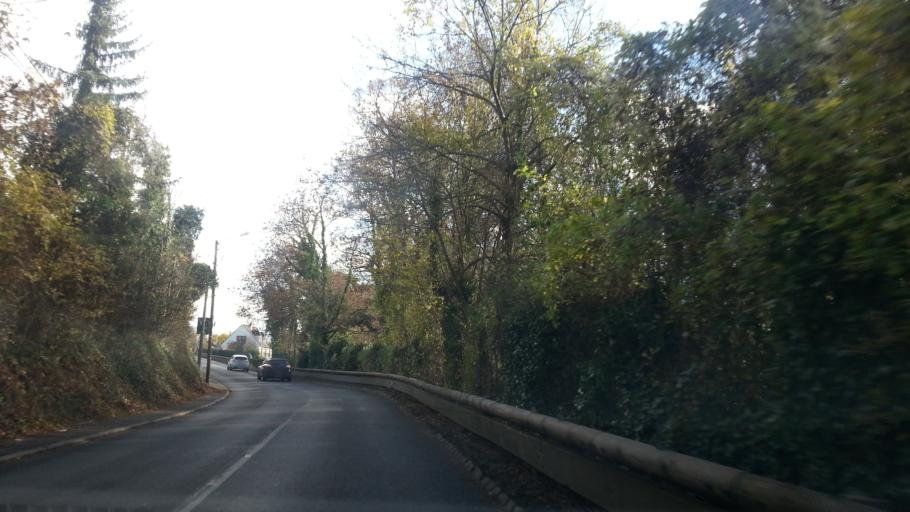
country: FR
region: Picardie
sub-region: Departement de l'Oise
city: Gouvieux
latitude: 49.2003
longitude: 2.4282
